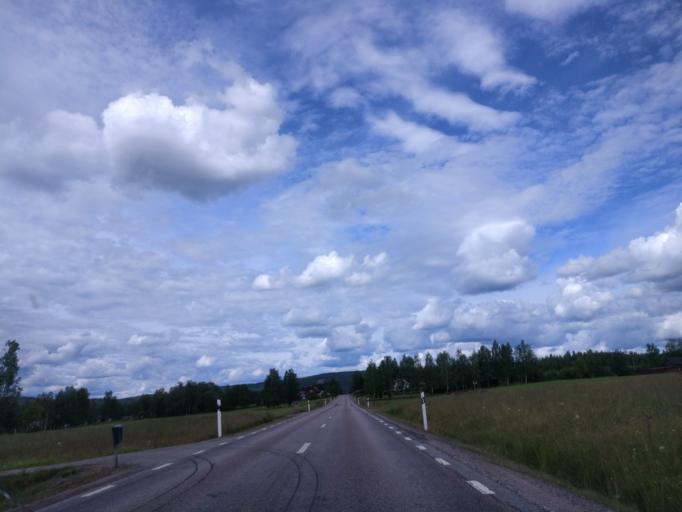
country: SE
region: Vaermland
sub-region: Hagfors Kommun
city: Ekshaerad
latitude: 60.1587
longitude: 13.4194
